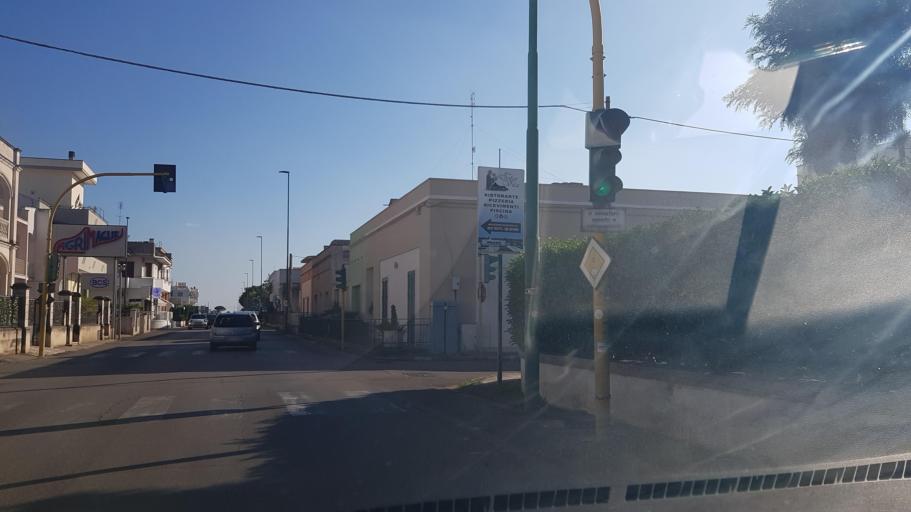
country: IT
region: Apulia
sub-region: Provincia di Lecce
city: Montesano Salentino
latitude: 39.9772
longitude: 18.3249
